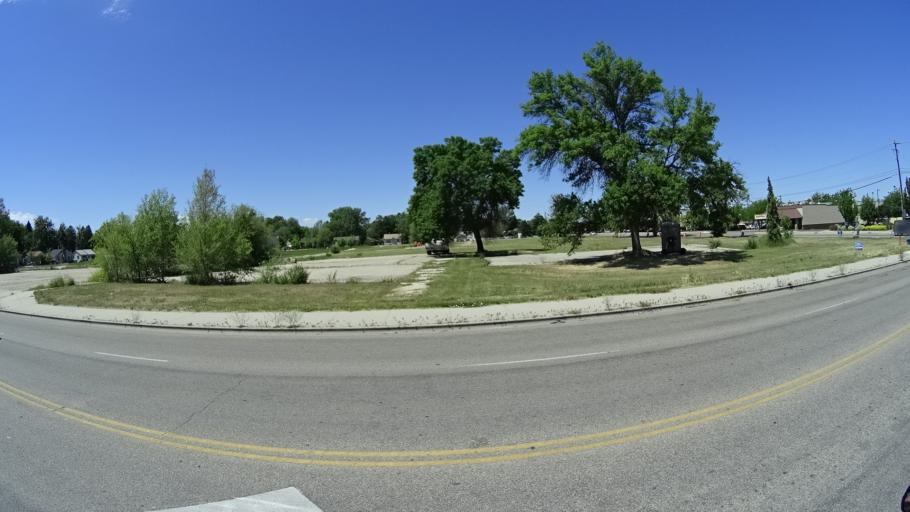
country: US
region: Idaho
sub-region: Ada County
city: Garden City
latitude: 43.6021
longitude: -116.2435
